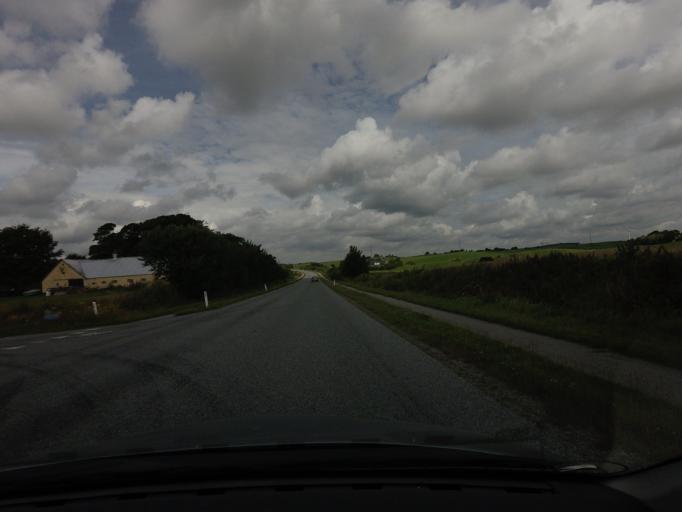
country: DK
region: North Denmark
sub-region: Hjorring Kommune
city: Tars
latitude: 57.3584
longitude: 10.2065
